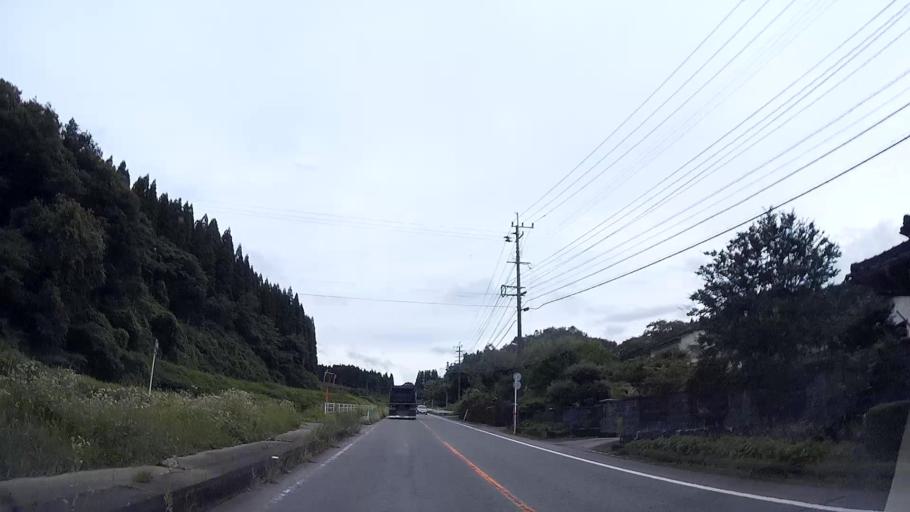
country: JP
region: Oita
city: Tsukawaki
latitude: 33.1251
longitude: 131.0392
